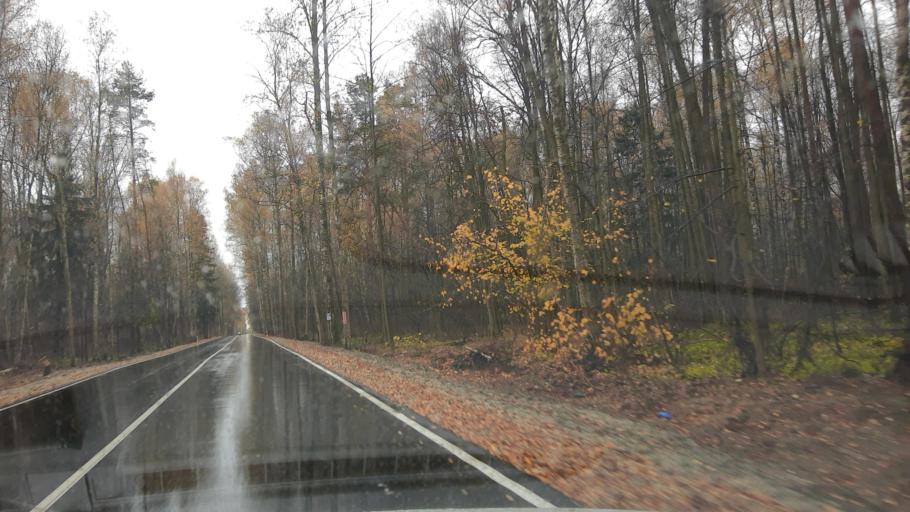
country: RU
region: Moskovskaya
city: Imeni Vorovskogo
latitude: 55.7927
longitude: 38.3682
